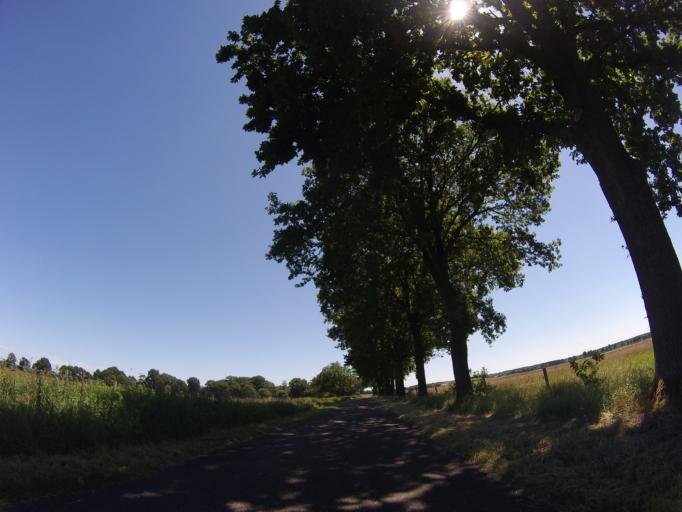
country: NL
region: Drenthe
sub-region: Gemeente Assen
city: Assen
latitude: 52.9445
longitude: 6.5733
